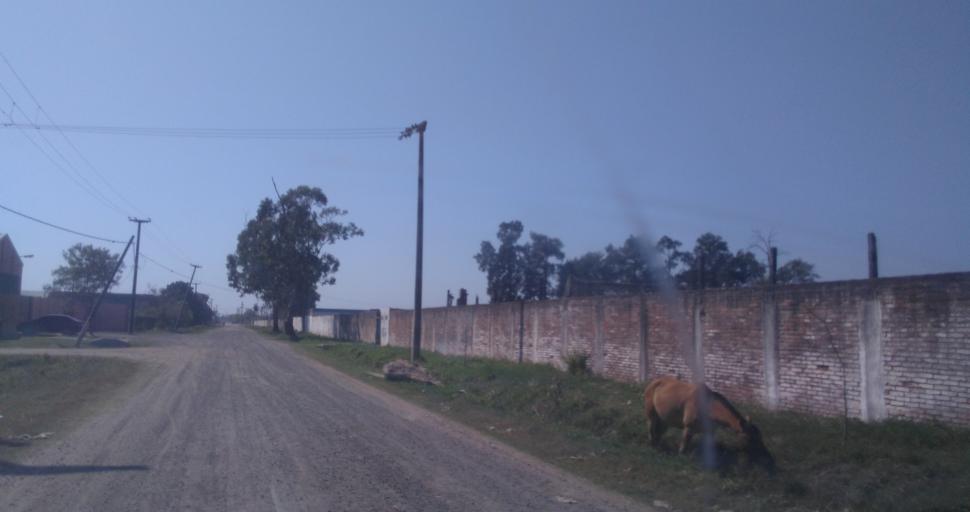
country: AR
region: Chaco
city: Fontana
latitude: -27.4339
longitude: -59.0264
